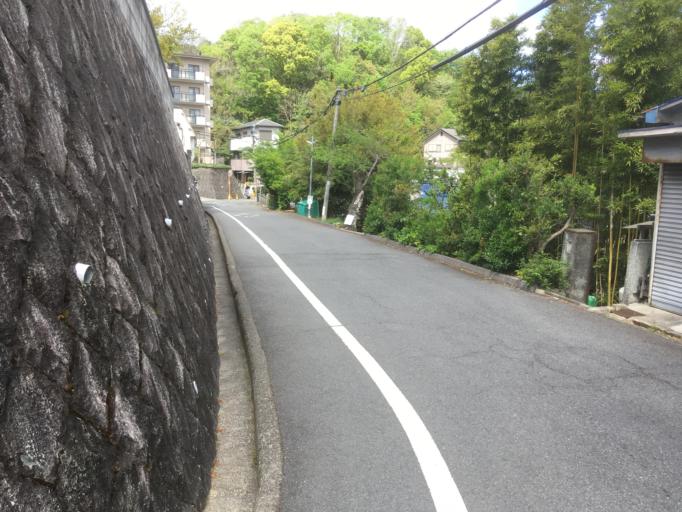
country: JP
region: Nara
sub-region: Ikoma-shi
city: Ikoma
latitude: 34.6994
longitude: 135.6921
